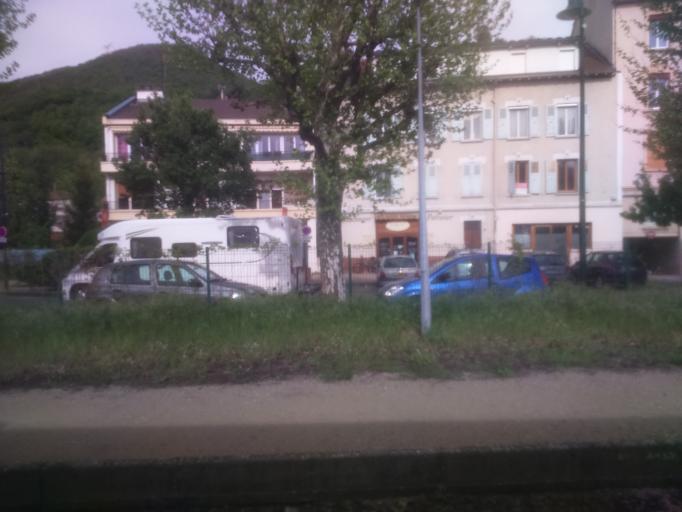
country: FR
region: Rhone-Alpes
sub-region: Departement de l'Isere
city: Champ-sur-Drac
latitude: 45.0850
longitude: 5.7426
